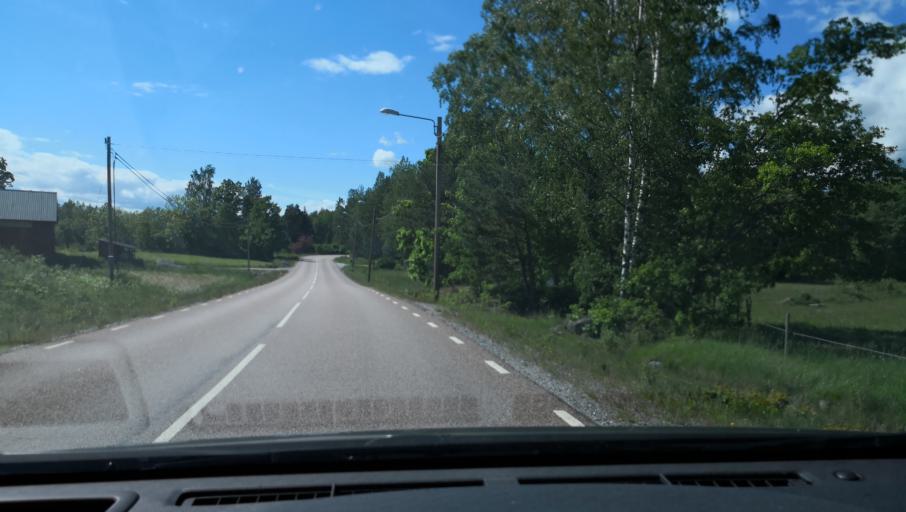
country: SE
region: Vaestmanland
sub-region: Kungsors Kommun
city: Kungsoer
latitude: 59.2904
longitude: 16.0598
